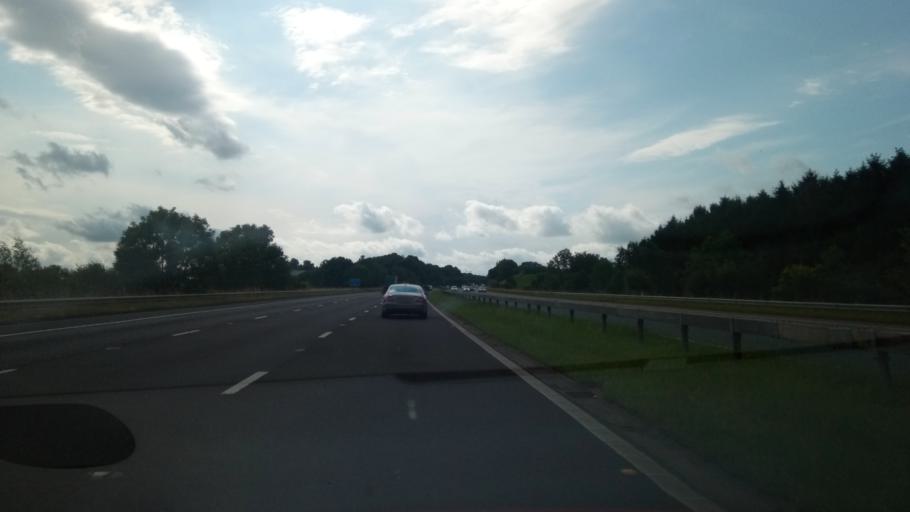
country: GB
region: England
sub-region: Cumbria
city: Penrith
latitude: 54.6410
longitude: -2.7343
